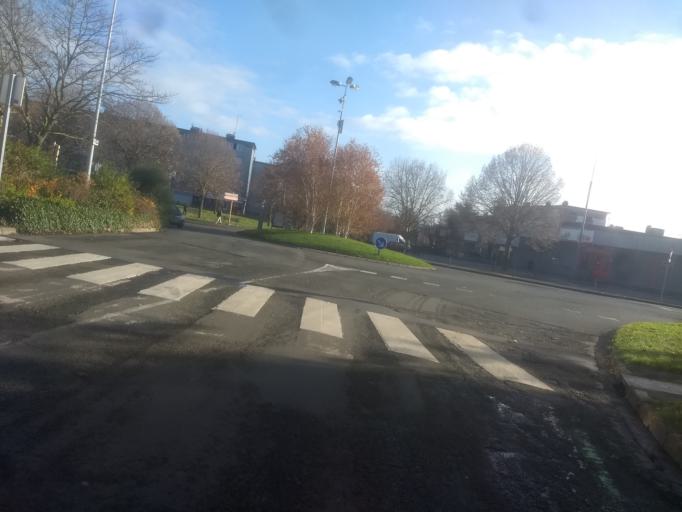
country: FR
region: Nord-Pas-de-Calais
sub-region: Departement du Pas-de-Calais
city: Anzin-Saint-Aubin
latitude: 50.3010
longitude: 2.7457
